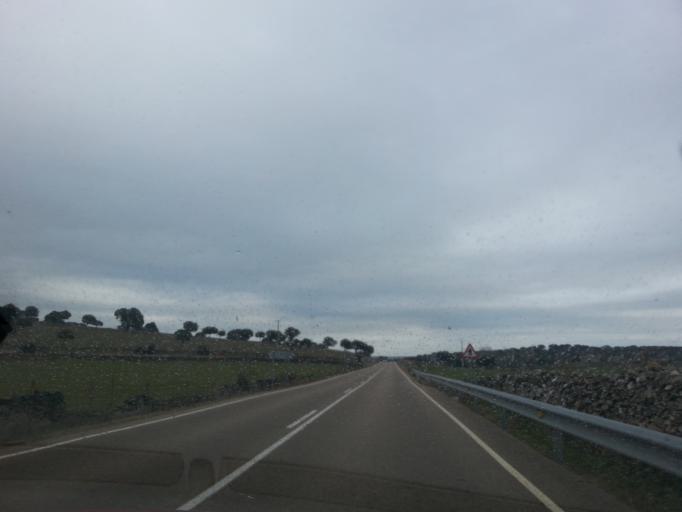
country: ES
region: Castille and Leon
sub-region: Provincia de Salamanca
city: Narros de Matalayegua
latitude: 40.7325
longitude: -5.9390
